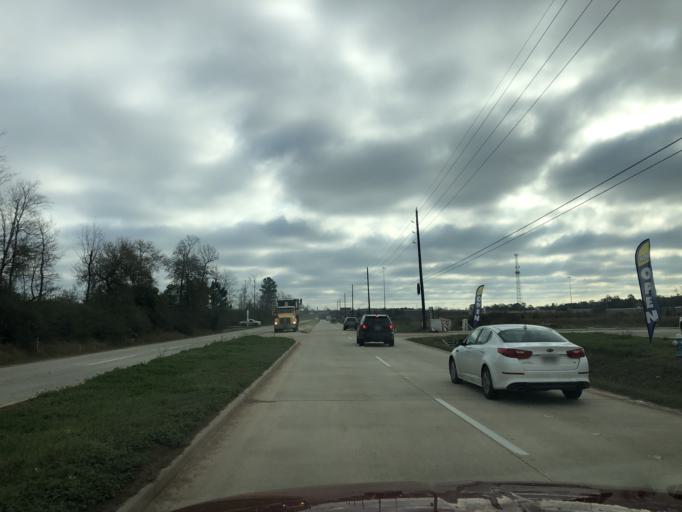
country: US
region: Texas
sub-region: Harris County
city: Spring
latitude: 30.0829
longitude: -95.4439
